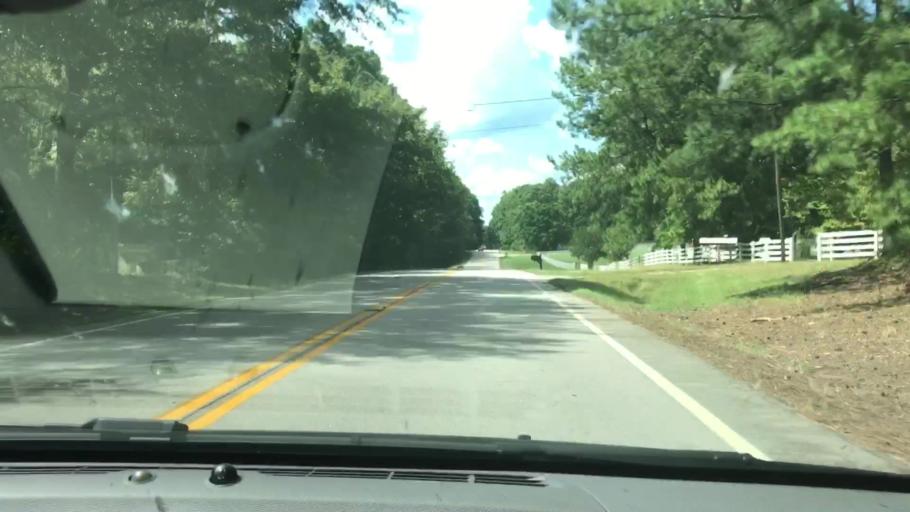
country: US
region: Georgia
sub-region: Troup County
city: La Grange
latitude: 33.1110
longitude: -85.0809
